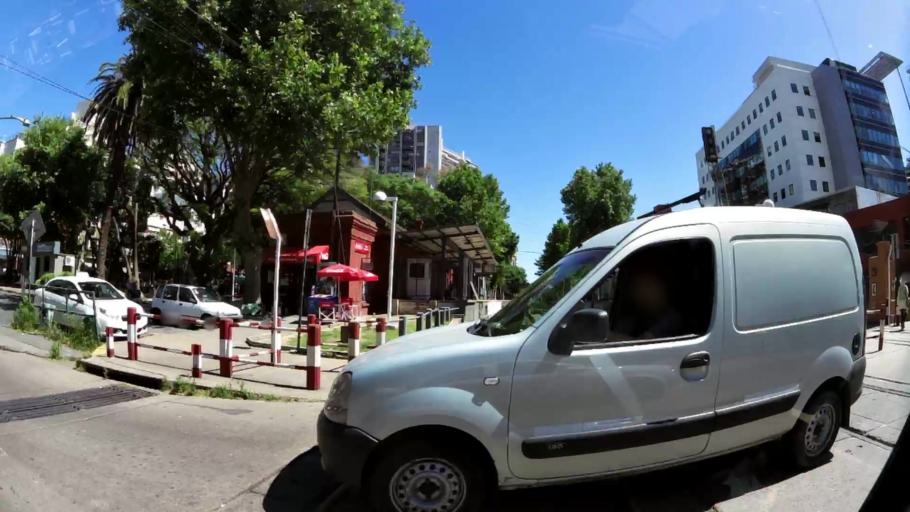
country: AR
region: Buenos Aires
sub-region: Partido de Vicente Lopez
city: Olivos
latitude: -34.5087
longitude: -58.4802
